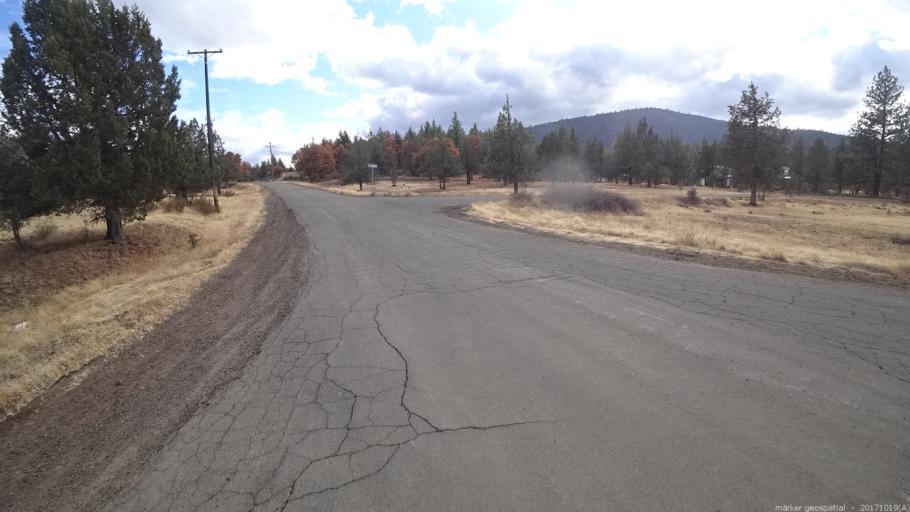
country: US
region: California
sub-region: Shasta County
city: Burney
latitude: 40.9784
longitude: -121.4457
